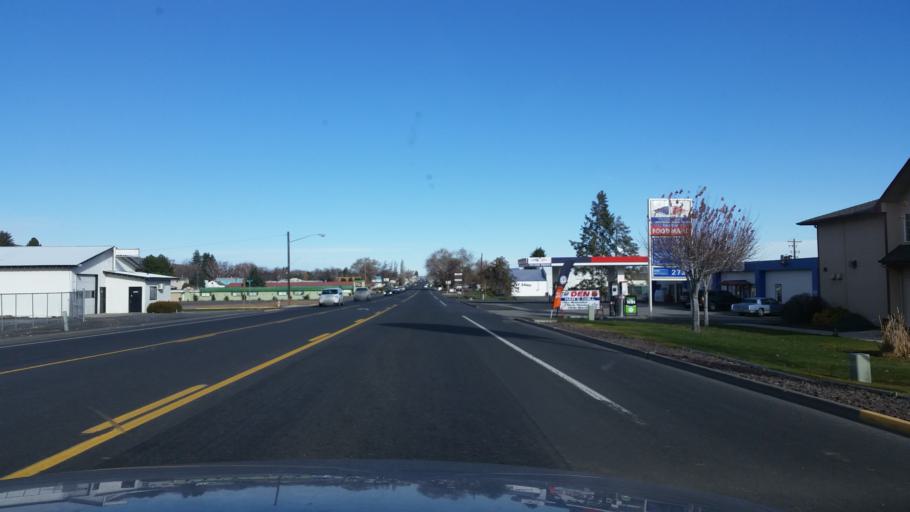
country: US
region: Washington
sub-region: Grant County
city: Ephrata
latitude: 47.3023
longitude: -119.5648
